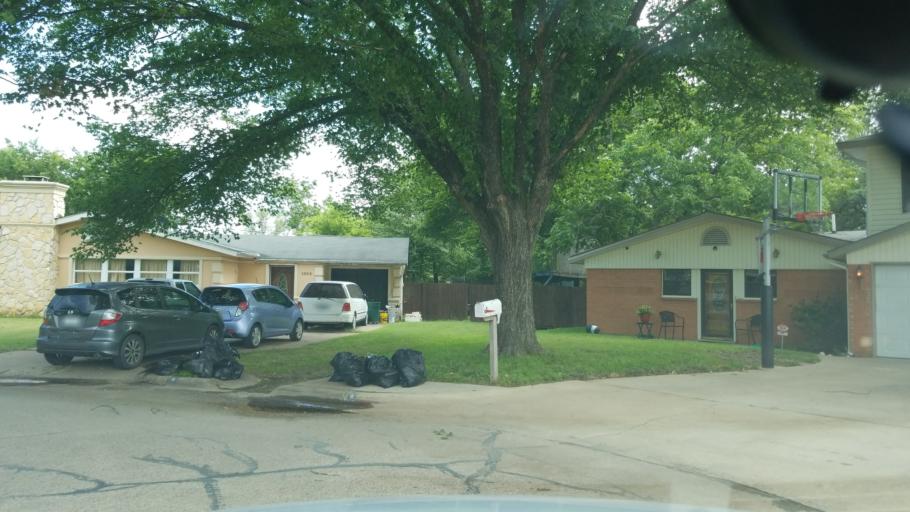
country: US
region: Texas
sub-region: Dallas County
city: Irving
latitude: 32.8326
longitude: -96.9490
